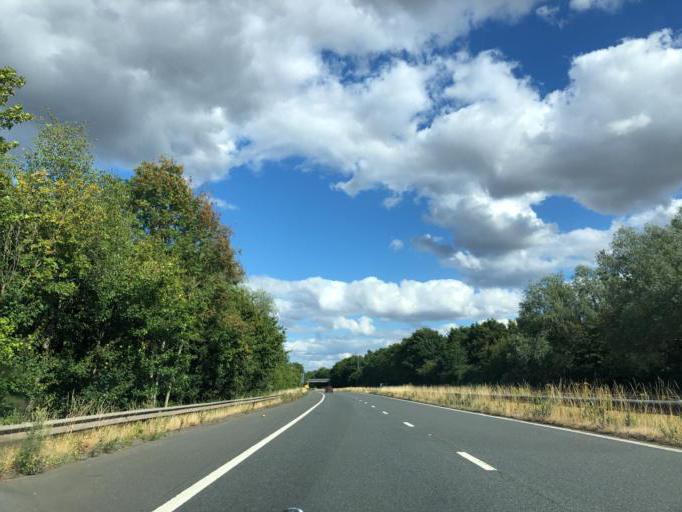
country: GB
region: England
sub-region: Warwickshire
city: Dunchurch
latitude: 52.3353
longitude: -1.3014
